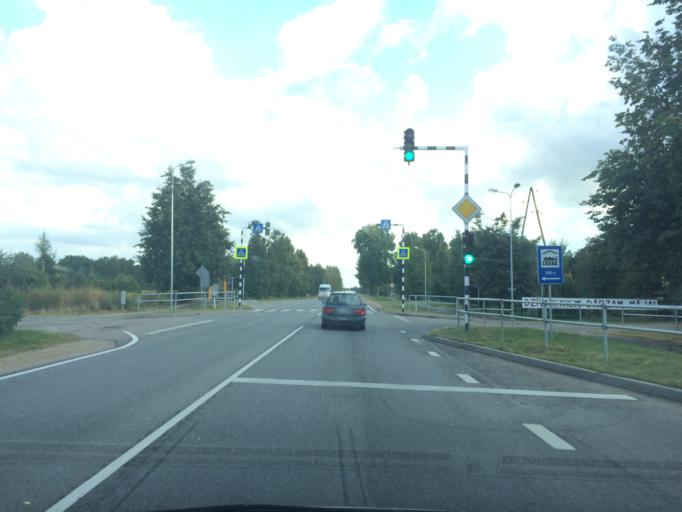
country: LV
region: Ogre
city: Ogre
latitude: 56.7809
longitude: 24.6512
